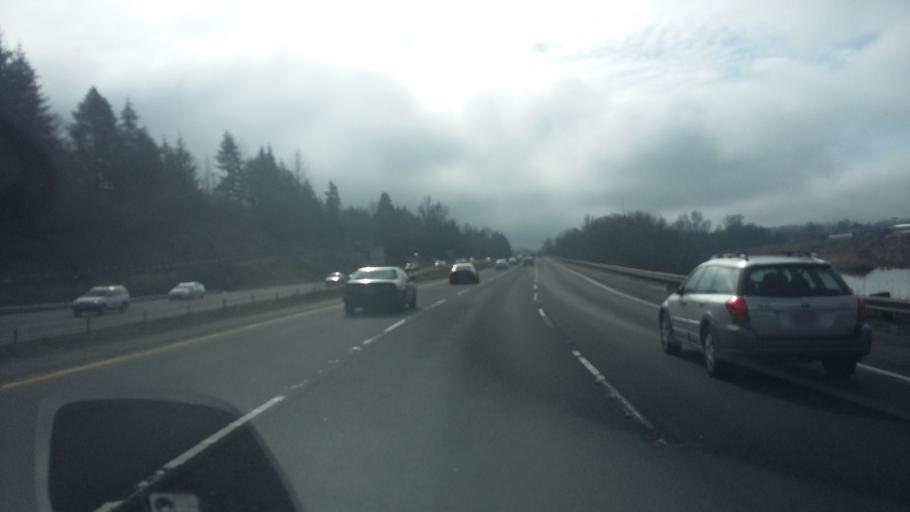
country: US
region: Washington
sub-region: Cowlitz County
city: Kelso
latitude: 46.1229
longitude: -122.8899
